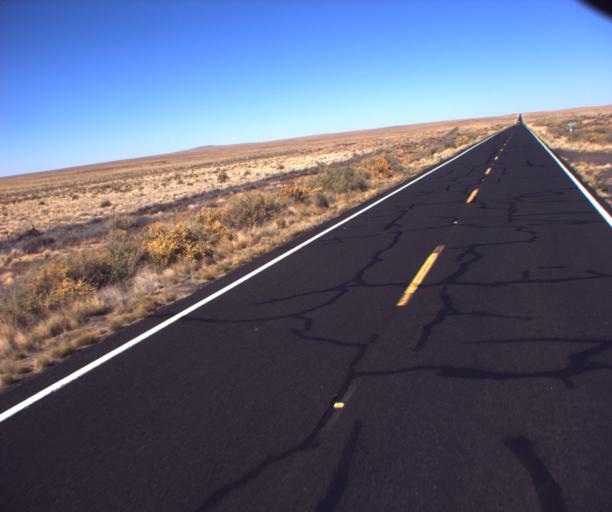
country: US
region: Arizona
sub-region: Navajo County
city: Dilkon
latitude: 35.5842
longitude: -110.4650
